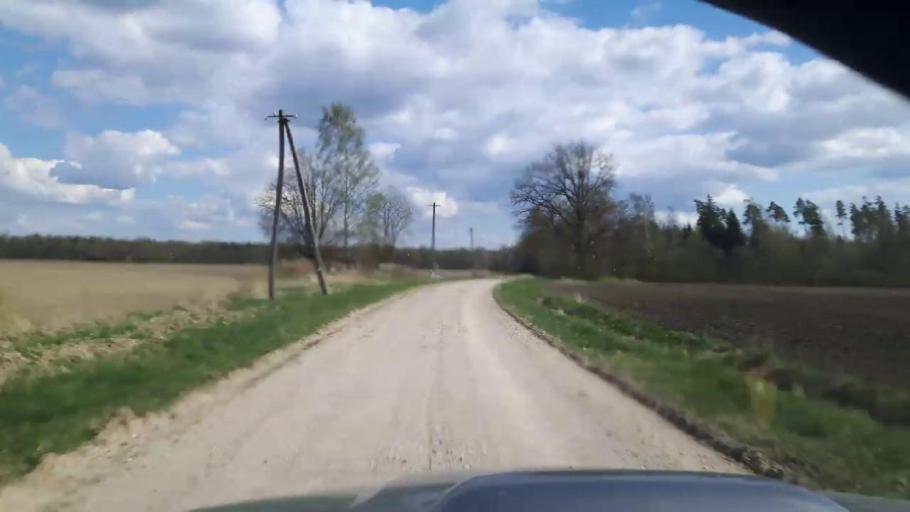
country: EE
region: Paernumaa
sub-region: Tootsi vald
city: Tootsi
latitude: 58.4585
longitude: 24.8072
